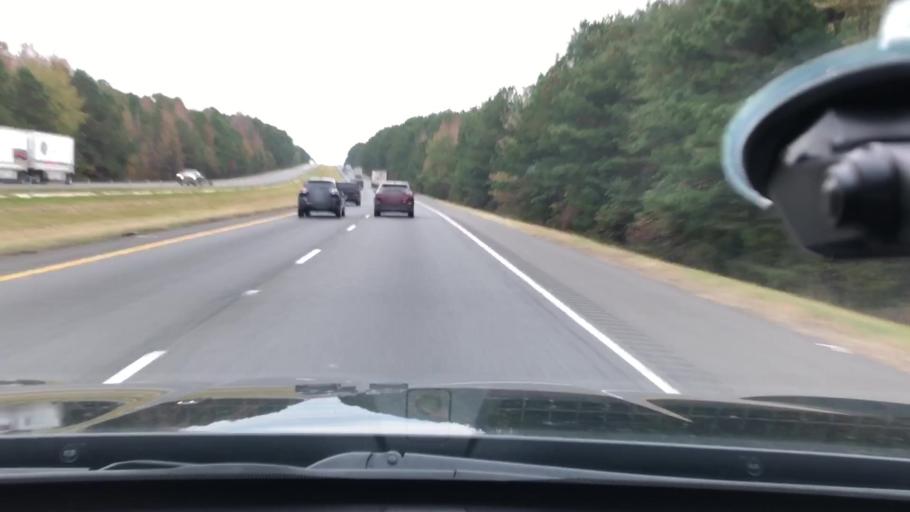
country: US
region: Arkansas
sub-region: Clark County
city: Gurdon
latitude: 34.0364
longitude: -93.1431
